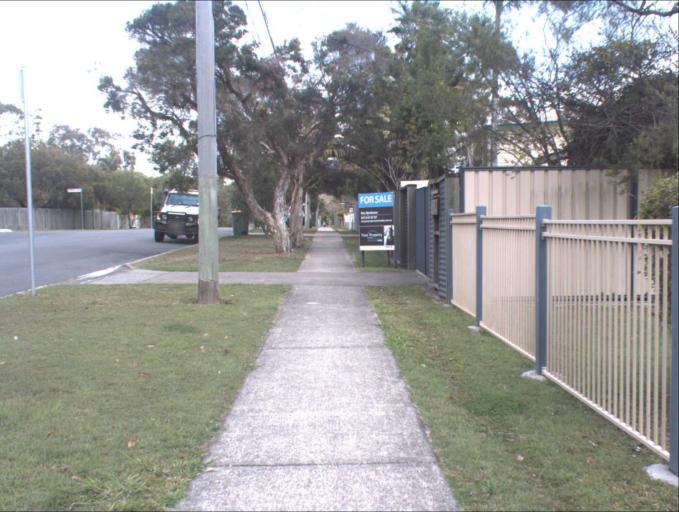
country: AU
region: Queensland
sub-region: Logan
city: Waterford West
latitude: -27.6720
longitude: 153.1350
